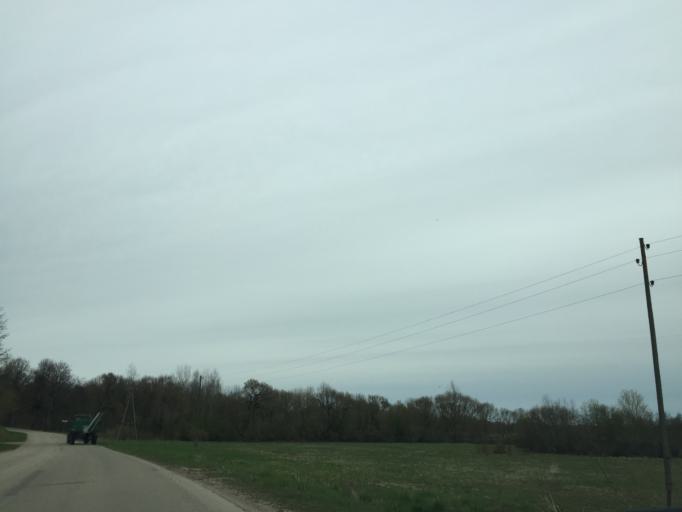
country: LV
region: Ludzas Rajons
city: Ludza
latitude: 56.5665
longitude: 27.7460
